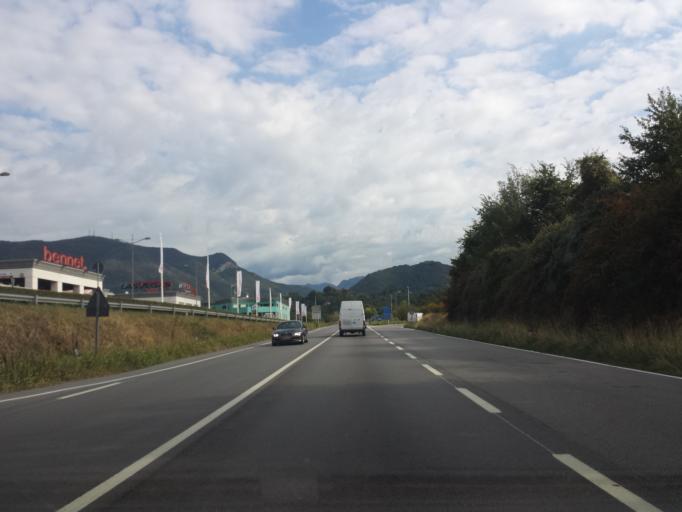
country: IT
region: Lombardy
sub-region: Provincia di Brescia
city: Gavardo-Sopraponte
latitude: 45.5759
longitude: 10.4443
